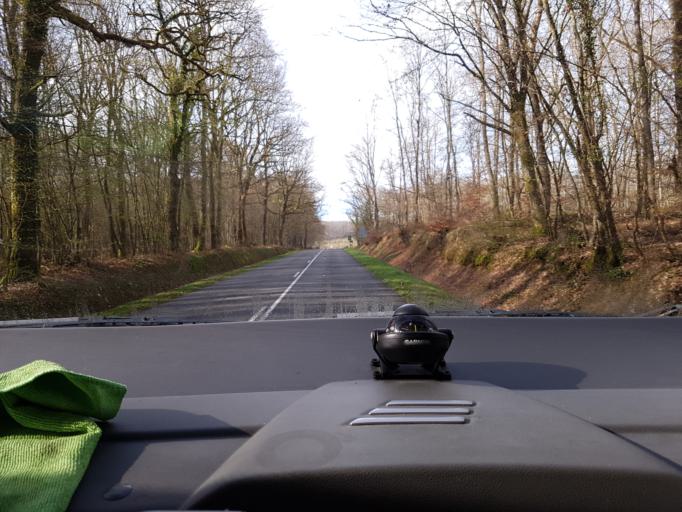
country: FR
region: Bourgogne
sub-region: Departement de Saone-et-Loire
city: Etang-sur-Arroux
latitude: 46.7949
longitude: 4.1497
